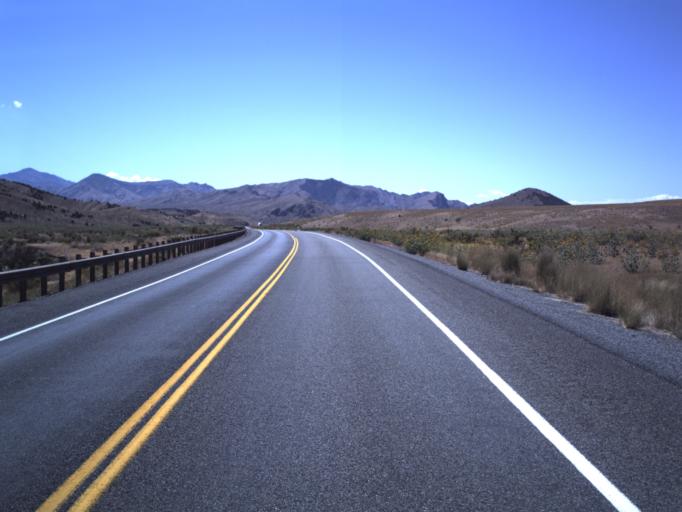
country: US
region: Utah
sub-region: Juab County
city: Nephi
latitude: 39.6271
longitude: -112.1212
